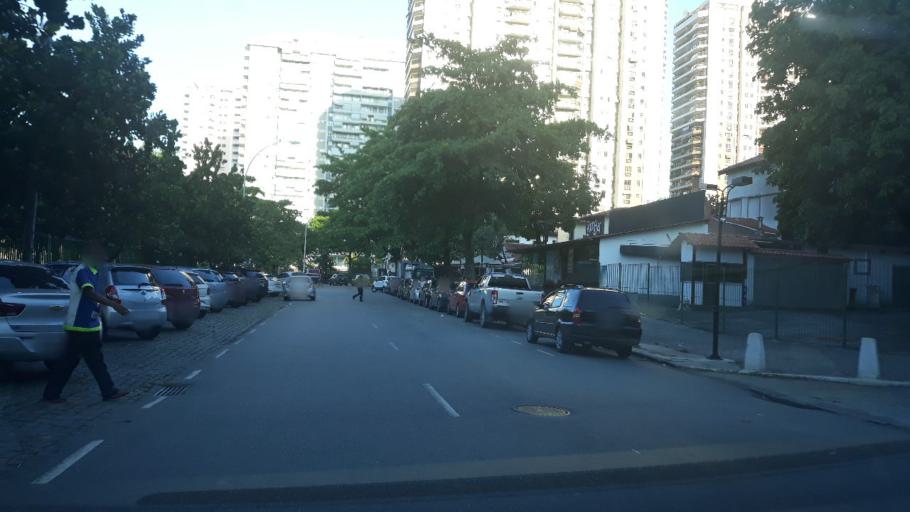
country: BR
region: Rio de Janeiro
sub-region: Rio De Janeiro
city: Rio de Janeiro
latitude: -23.0023
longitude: -43.3509
